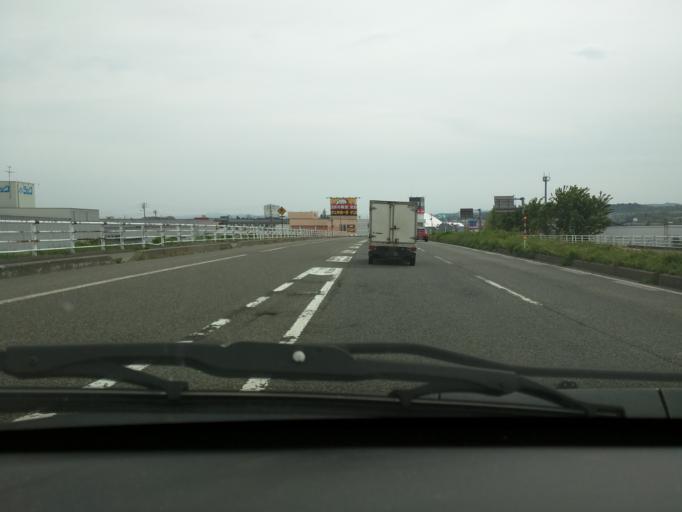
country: JP
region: Niigata
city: Nagaoka
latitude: 37.4492
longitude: 138.8000
